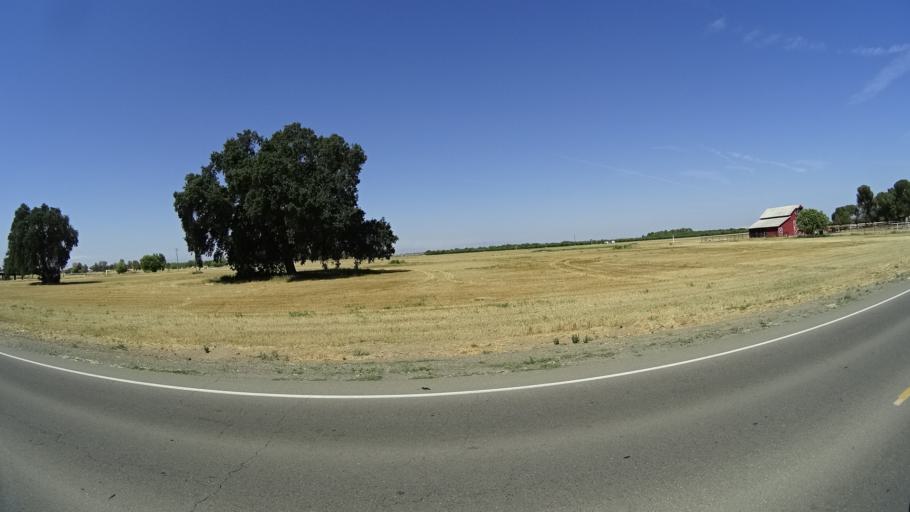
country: US
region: California
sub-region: Kings County
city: Lemoore
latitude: 36.2631
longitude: -119.7809
